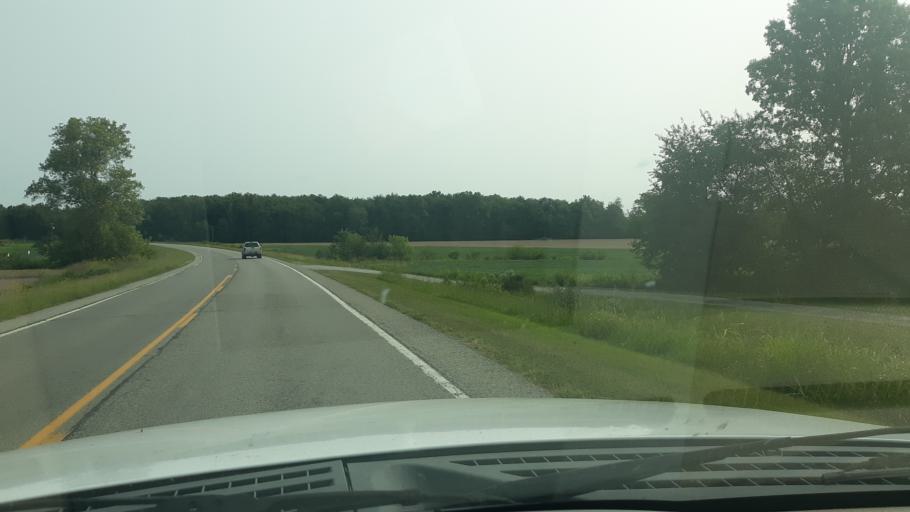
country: US
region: Illinois
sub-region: White County
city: Norris City
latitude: 37.9678
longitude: -88.3248
